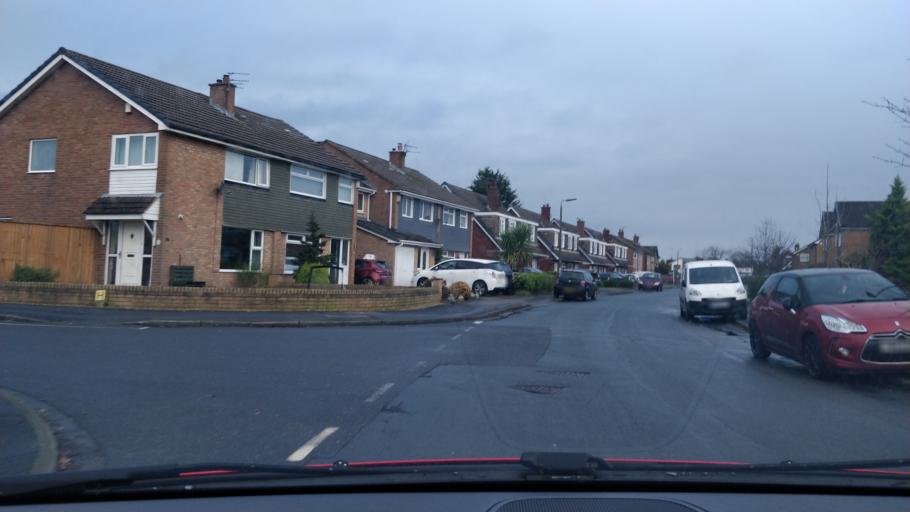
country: GB
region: England
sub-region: Lancashire
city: Preston
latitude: 53.7412
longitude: -2.7378
